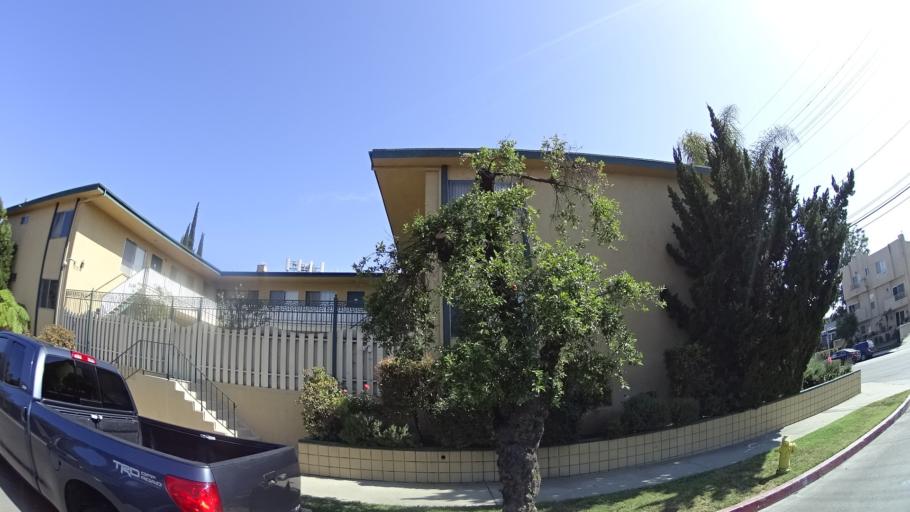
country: US
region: California
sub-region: Los Angeles County
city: Sherman Oaks
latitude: 34.1604
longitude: -118.4571
